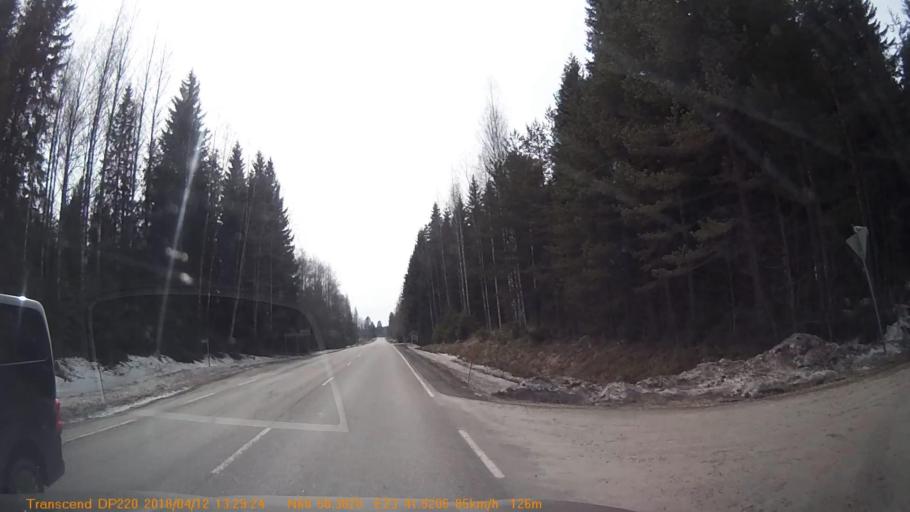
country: FI
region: Haeme
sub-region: Forssa
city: Forssa
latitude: 60.9729
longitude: 23.6918
